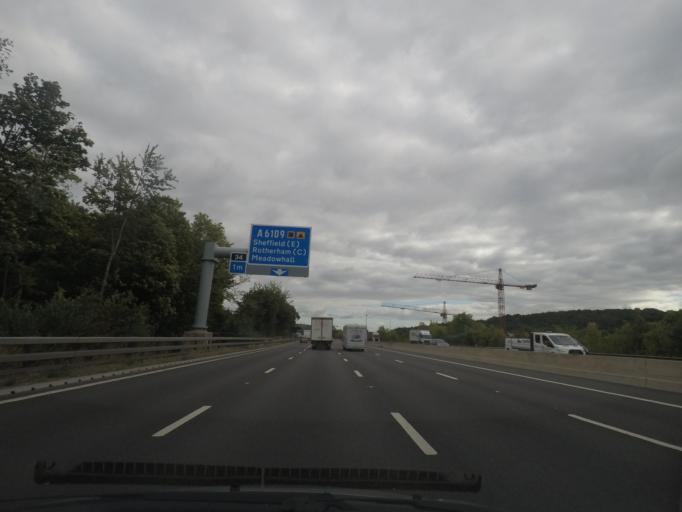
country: GB
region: England
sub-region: Rotherham
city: Wentworth
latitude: 53.4379
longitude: -1.4331
